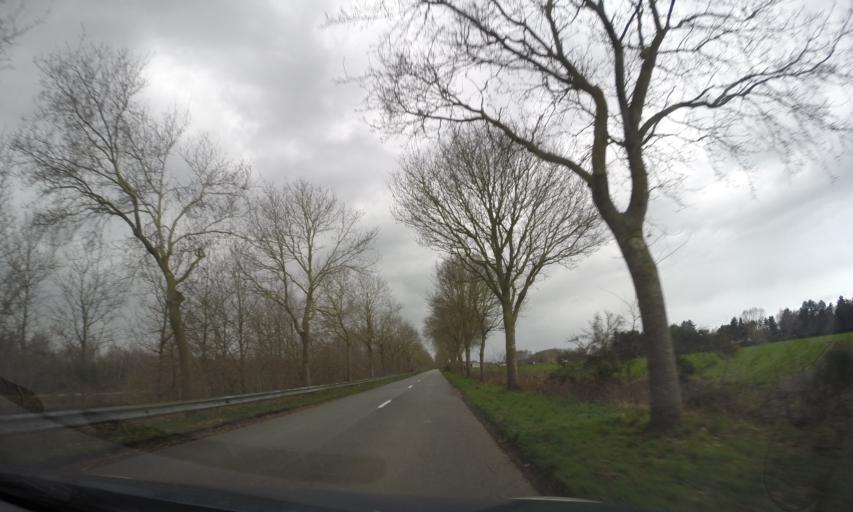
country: BE
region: Flanders
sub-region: Provincie West-Vlaanderen
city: Beernem
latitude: 51.1322
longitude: 3.3564
